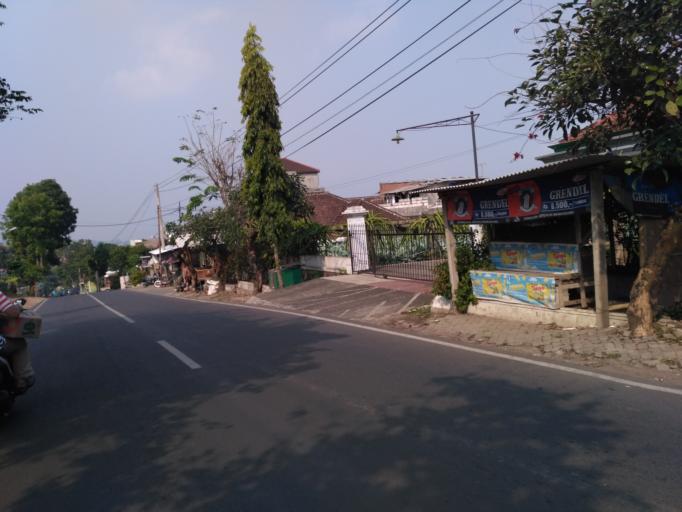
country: ID
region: East Java
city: Batu
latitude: -7.8647
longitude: 112.5439
